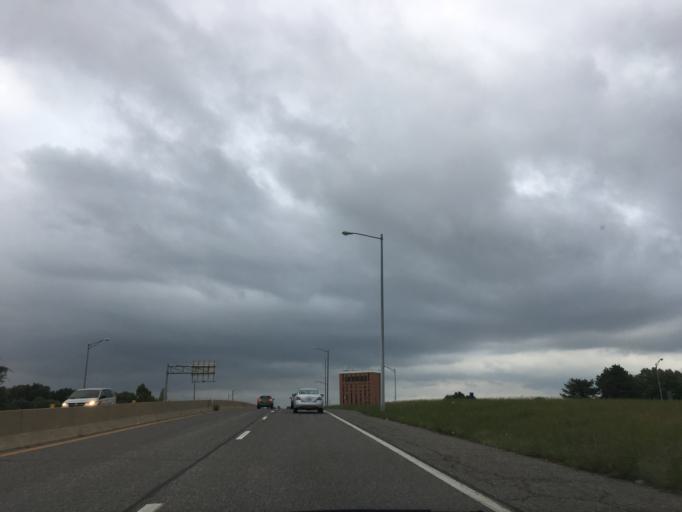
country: US
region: Missouri
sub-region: Saint Louis County
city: Saint Ann
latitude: 38.7418
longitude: -90.3960
